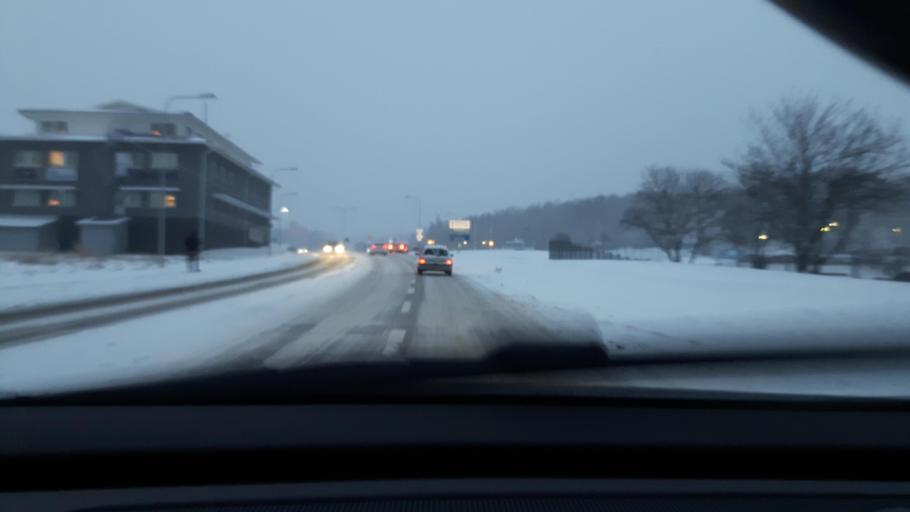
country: SE
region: Vaestra Goetaland
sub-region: Goteborg
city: Majorna
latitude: 57.6483
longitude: 11.9520
